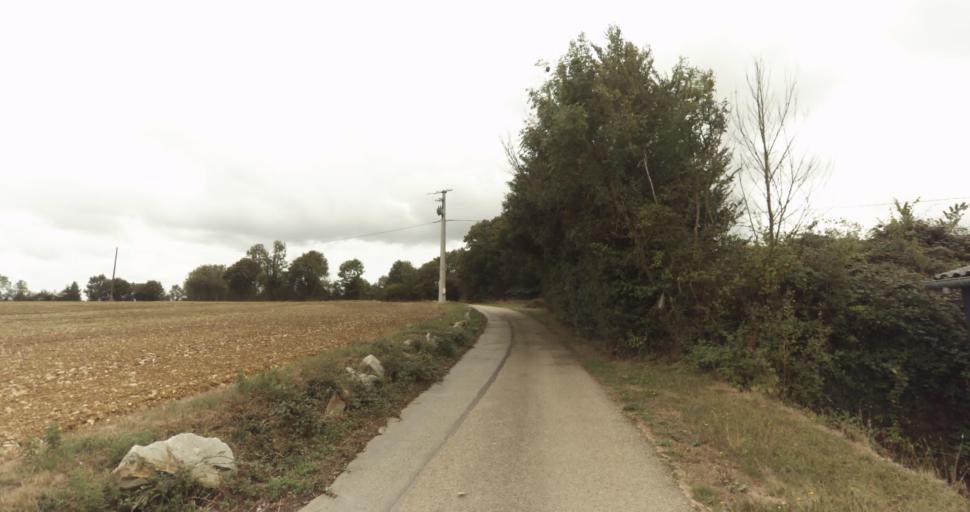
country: FR
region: Lower Normandy
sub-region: Departement de l'Orne
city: Gace
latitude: 48.8207
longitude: 0.3683
